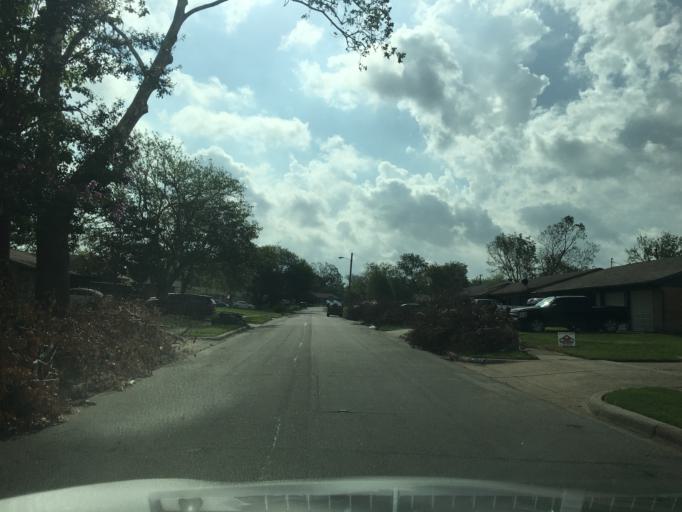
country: US
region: Texas
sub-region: Dallas County
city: Richardson
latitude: 32.9022
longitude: -96.7560
